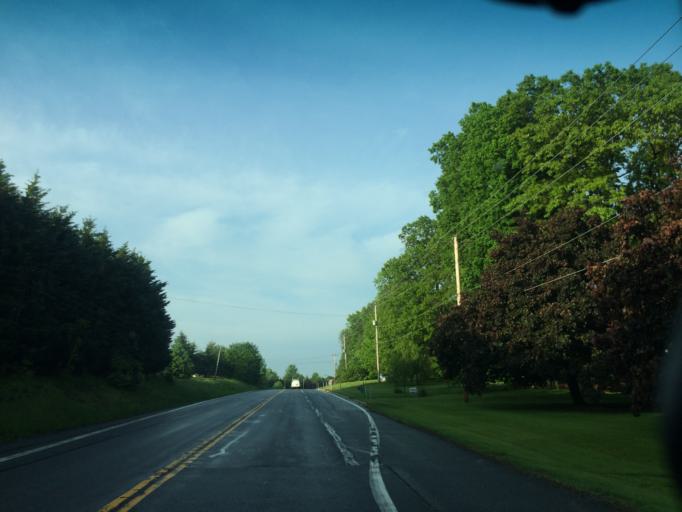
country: US
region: Maryland
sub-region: Carroll County
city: Mount Airy
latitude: 39.4071
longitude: -77.1294
